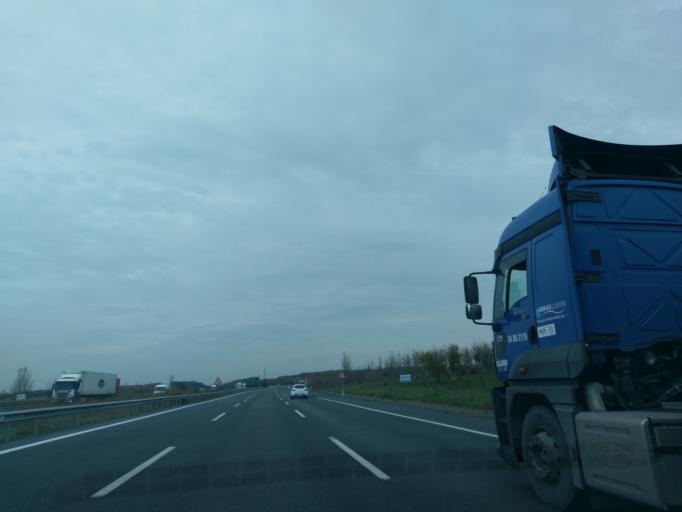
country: TR
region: Istanbul
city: Canta
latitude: 41.1764
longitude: 28.1159
